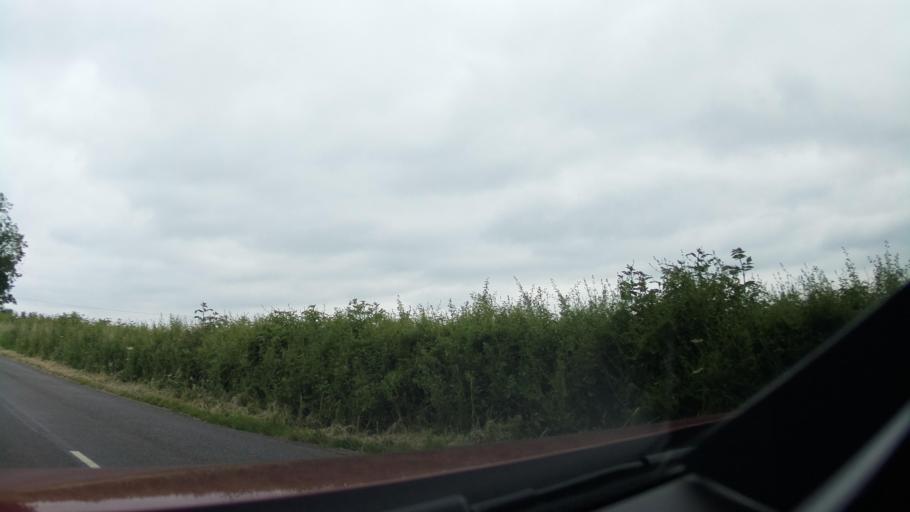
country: GB
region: England
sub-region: Leicestershire
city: Melton Mowbray
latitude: 52.7157
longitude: -0.8297
